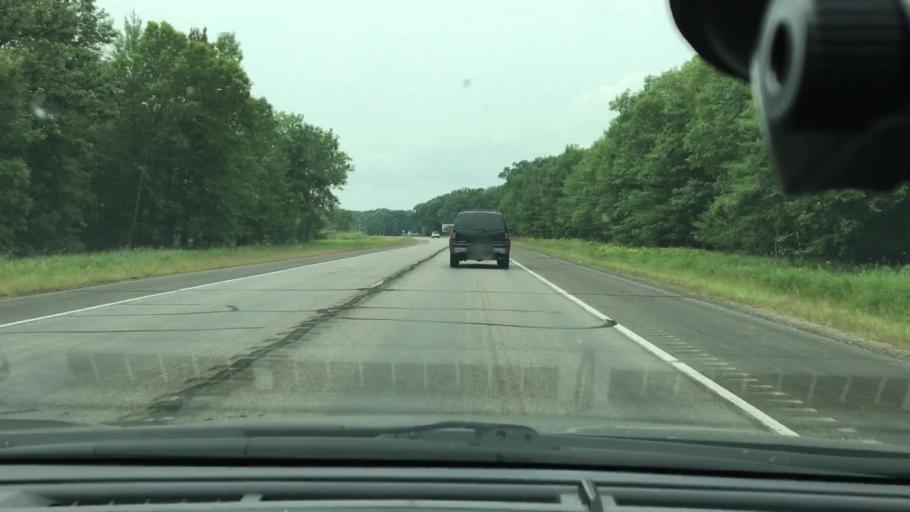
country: US
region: Minnesota
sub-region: Mille Lacs County
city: Vineland
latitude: 46.3244
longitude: -93.7962
